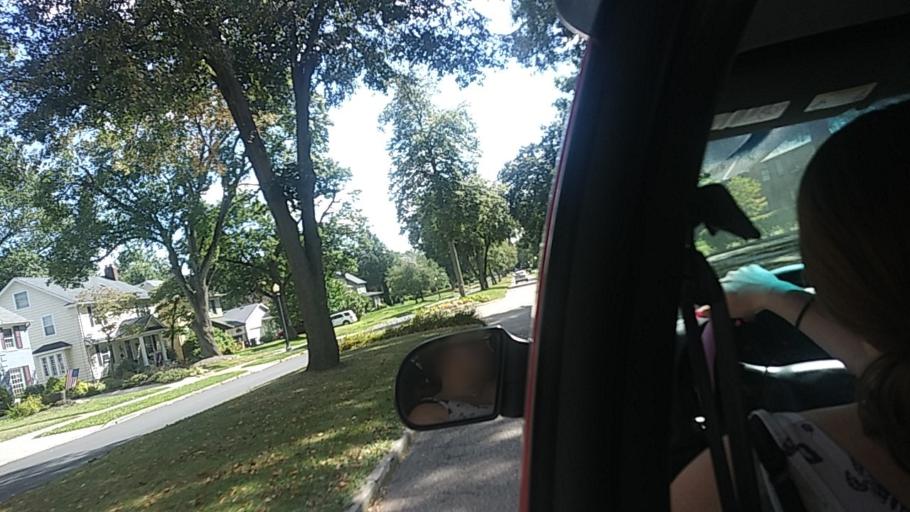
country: US
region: Ohio
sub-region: Summit County
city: Akron
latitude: 41.1104
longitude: -81.5615
